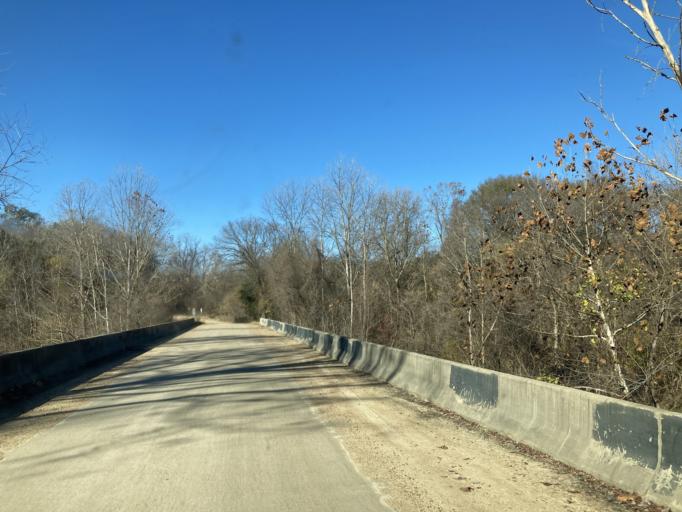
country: US
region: Mississippi
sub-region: Yazoo County
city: Yazoo City
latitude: 32.7063
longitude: -90.4694
